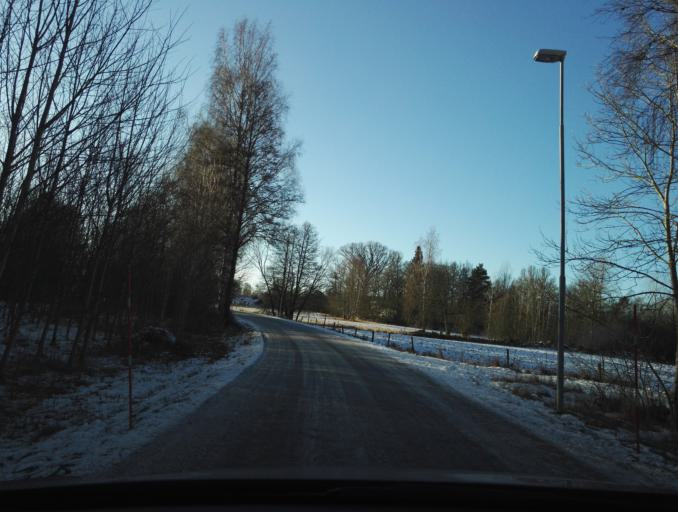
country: SE
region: Kronoberg
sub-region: Vaxjo Kommun
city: Gemla
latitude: 56.8295
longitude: 14.5872
